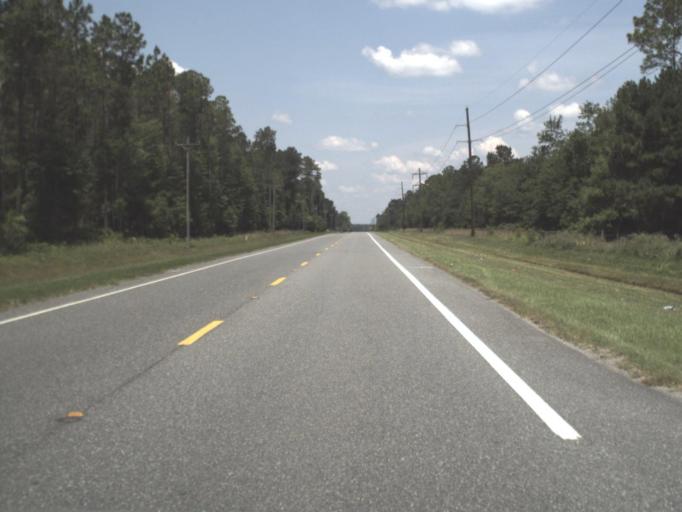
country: US
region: Florida
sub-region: Union County
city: Lake Butler
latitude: 29.9881
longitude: -82.2565
